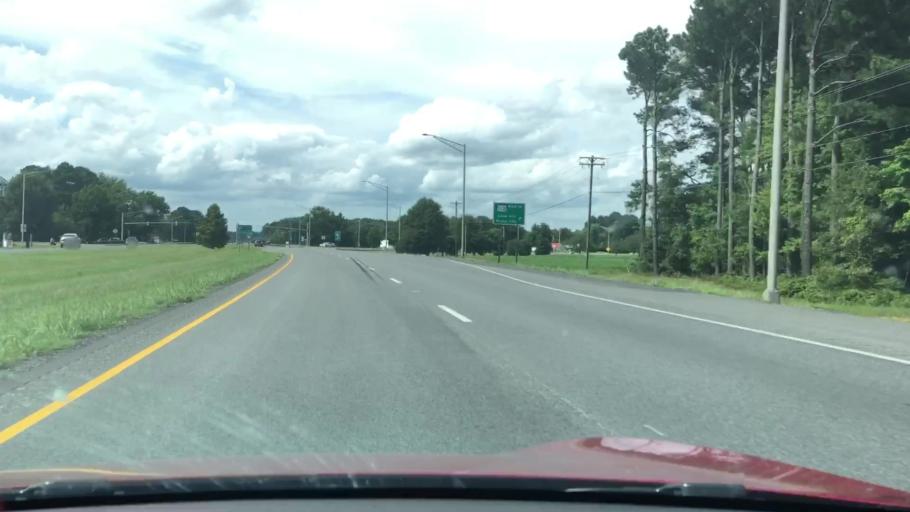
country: US
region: Maryland
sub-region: Worcester County
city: Pocomoke City
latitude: 38.0637
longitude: -75.5455
